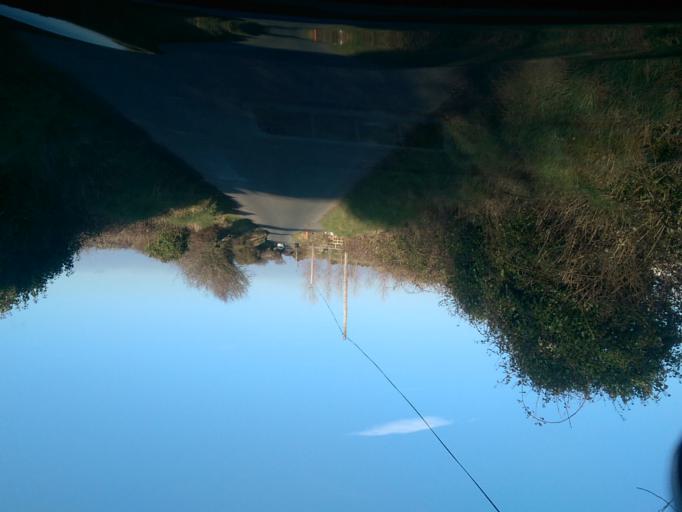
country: IE
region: Connaught
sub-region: County Galway
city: Oranmore
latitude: 53.2111
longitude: -8.8892
